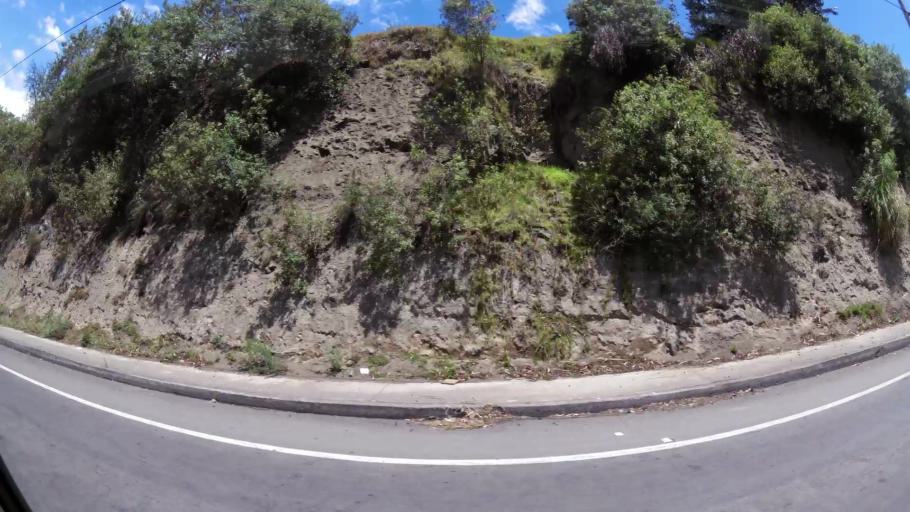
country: EC
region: Tungurahua
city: Pelileo
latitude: -1.3242
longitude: -78.5957
